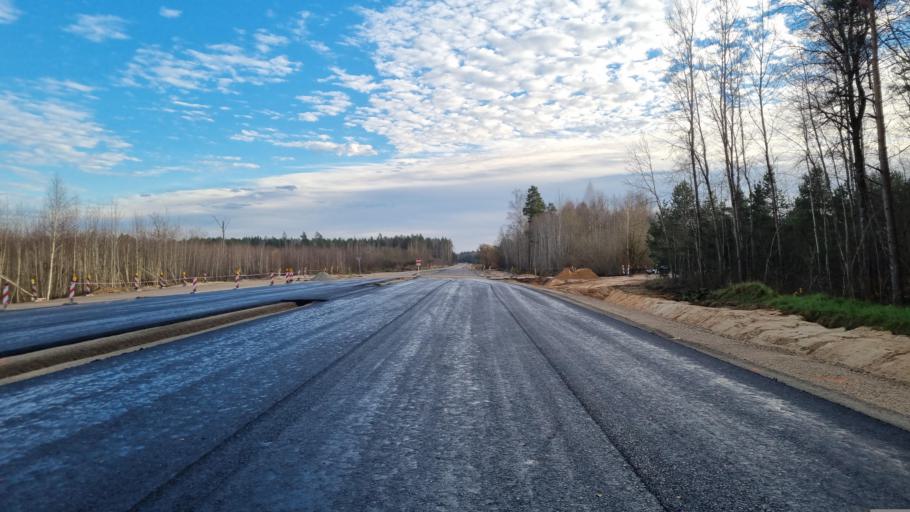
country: LV
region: Kekava
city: Kekava
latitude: 56.8044
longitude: 24.2002
